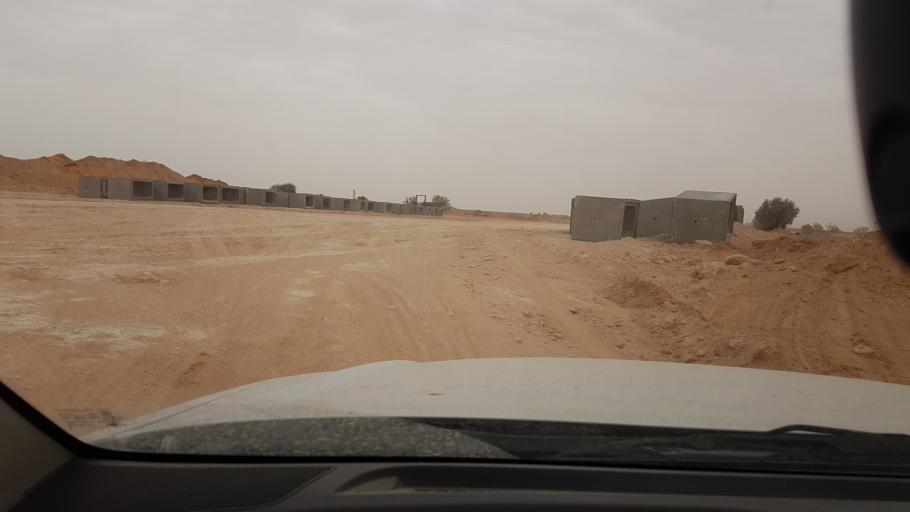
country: TN
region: Madanin
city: Medenine
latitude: 33.3197
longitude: 10.6039
